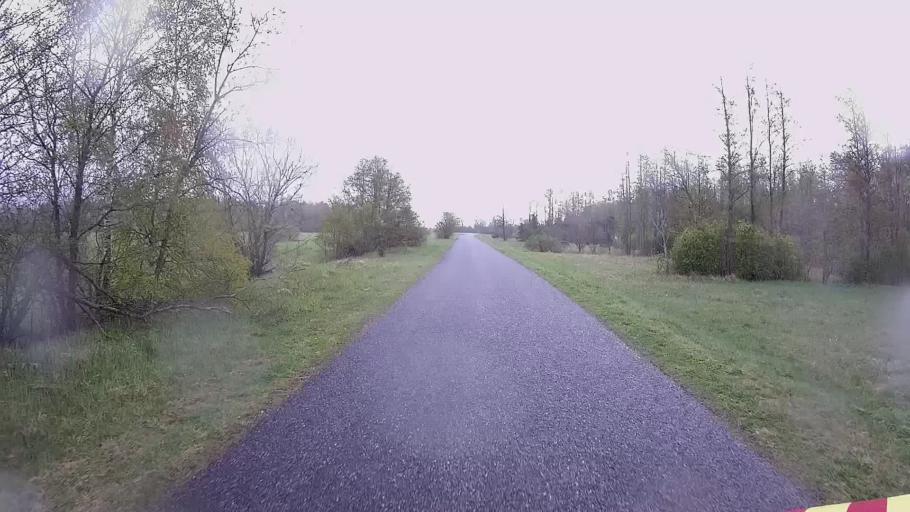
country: EE
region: Hiiumaa
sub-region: Kaerdla linn
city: Kardla
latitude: 58.6965
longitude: 22.5482
